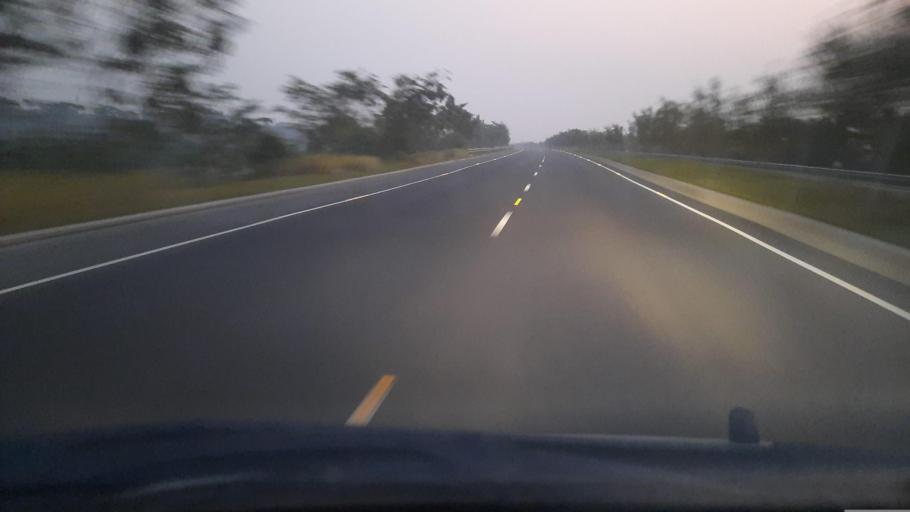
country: BD
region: Dhaka
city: Char Bhadrasan
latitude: 23.3991
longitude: 90.2407
